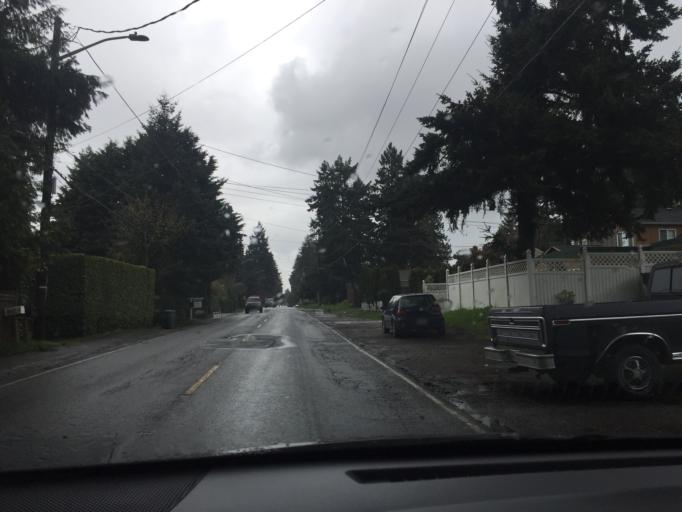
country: US
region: Washington
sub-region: King County
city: Lake Forest Park
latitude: 47.7255
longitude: -122.2964
